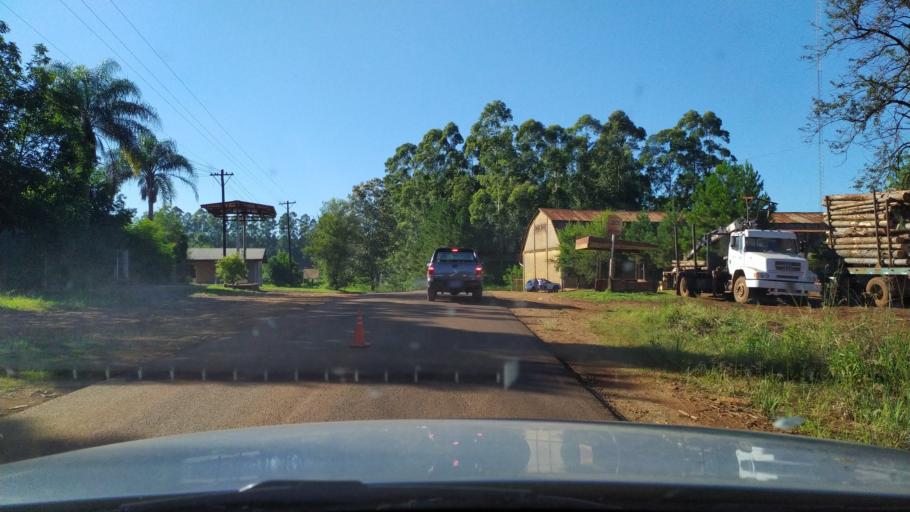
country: AR
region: Misiones
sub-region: Departamento de Montecarlo
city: Montecarlo
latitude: -26.6058
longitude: -54.7009
